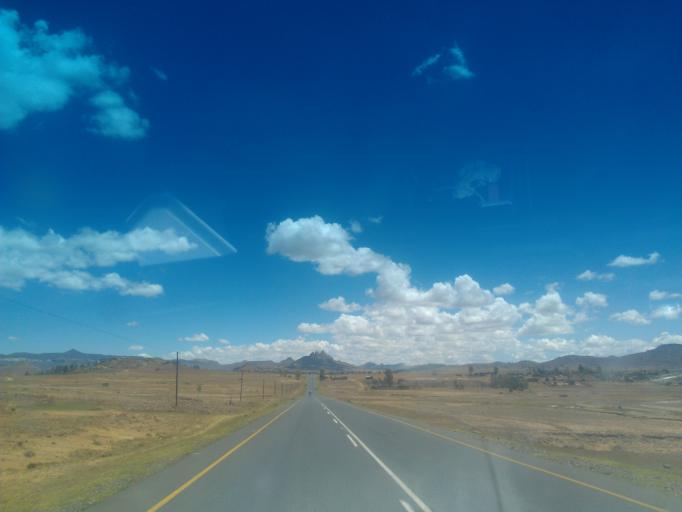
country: LS
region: Mafeteng
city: Mafeteng
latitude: -29.6710
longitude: 27.4507
